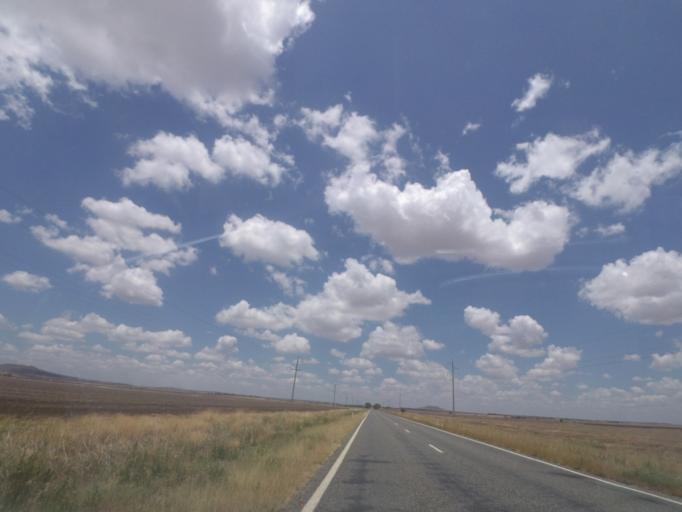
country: AU
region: Queensland
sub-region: Toowoomba
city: Top Camp
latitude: -27.9086
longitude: 151.9788
